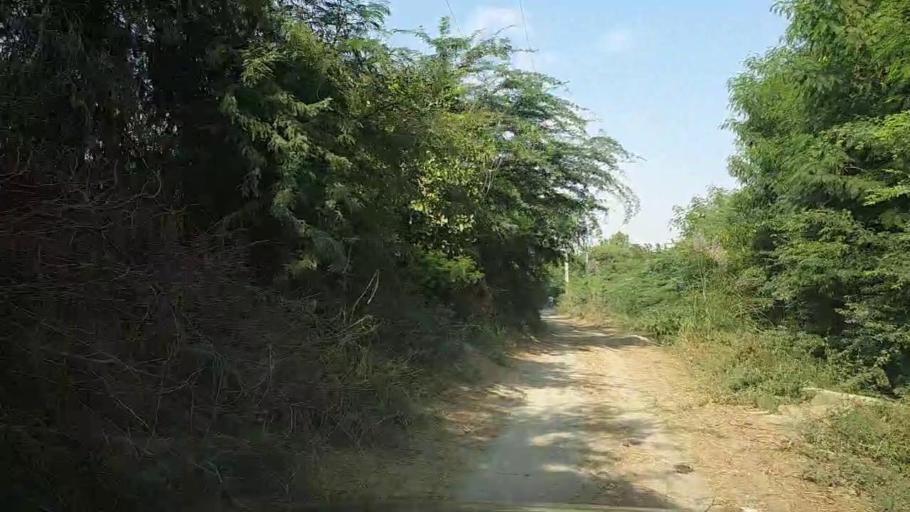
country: PK
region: Sindh
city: Thatta
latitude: 24.7950
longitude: 67.8222
